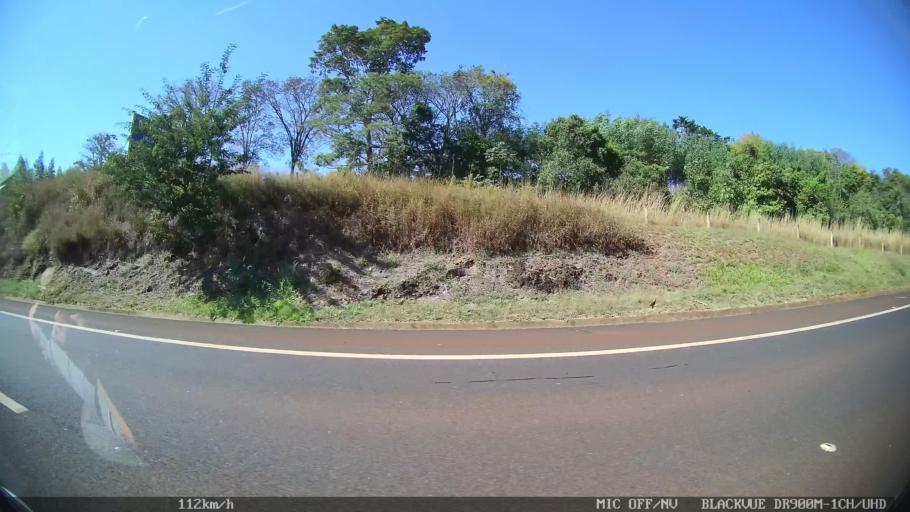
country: BR
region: Sao Paulo
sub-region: Franca
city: Franca
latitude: -20.6192
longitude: -47.4586
